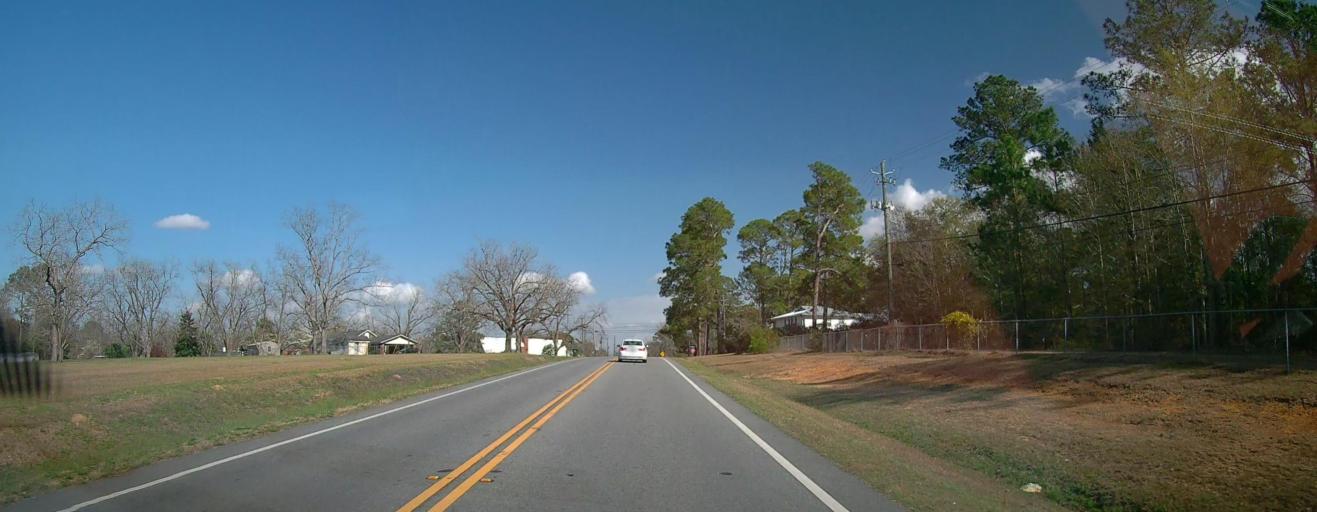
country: US
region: Georgia
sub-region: Dodge County
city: Eastman
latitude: 32.1963
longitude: -83.1888
